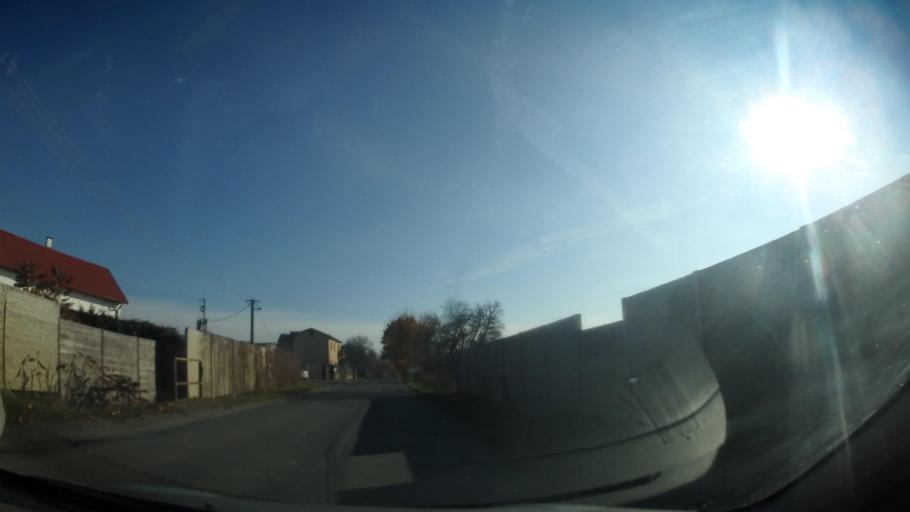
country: CZ
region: Central Bohemia
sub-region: Okres Praha-Vychod
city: Strancice
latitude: 49.9576
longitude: 14.6888
